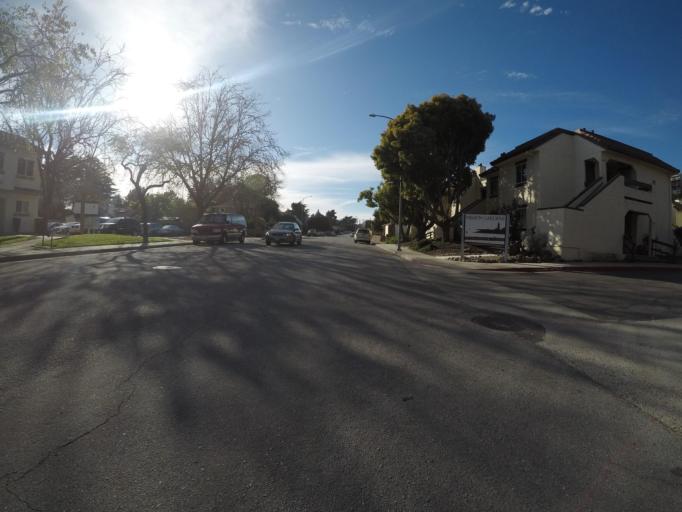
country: US
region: California
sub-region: Santa Cruz County
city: Santa Cruz
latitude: 36.9613
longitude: -122.0530
